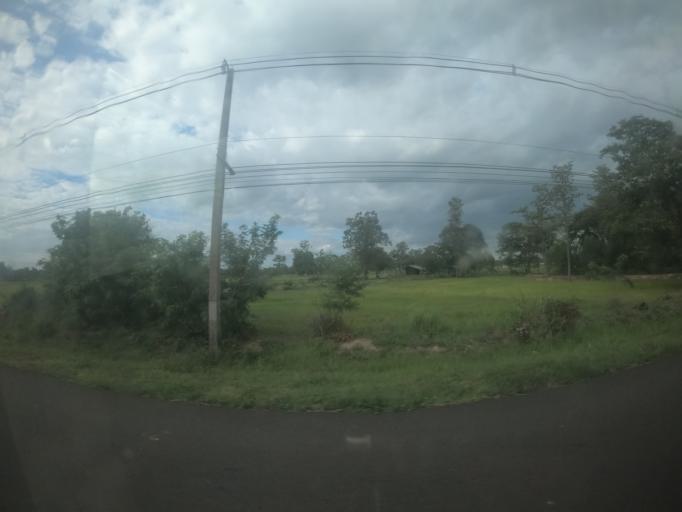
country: TH
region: Surin
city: Kap Choeng
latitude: 14.5585
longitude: 103.5011
